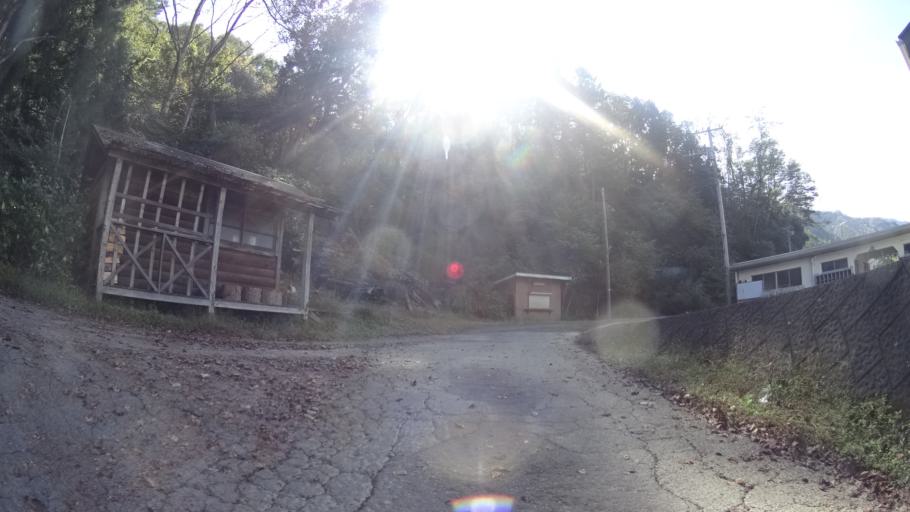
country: JP
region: Yamanashi
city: Uenohara
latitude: 35.5743
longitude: 139.0361
